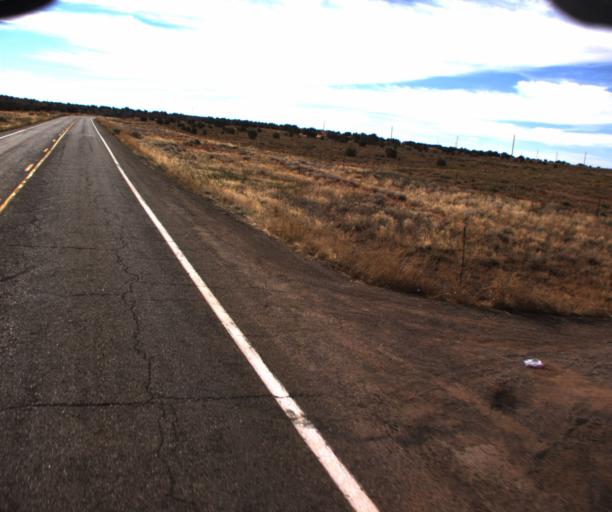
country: US
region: Arizona
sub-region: Coconino County
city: Kaibito
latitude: 36.6849
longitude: -111.2561
